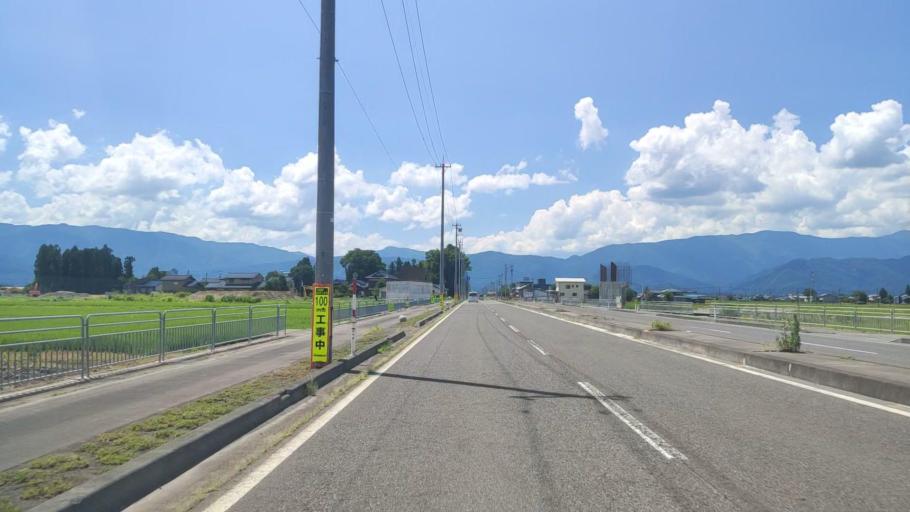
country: JP
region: Fukui
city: Ono
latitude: 35.9990
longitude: 136.5091
